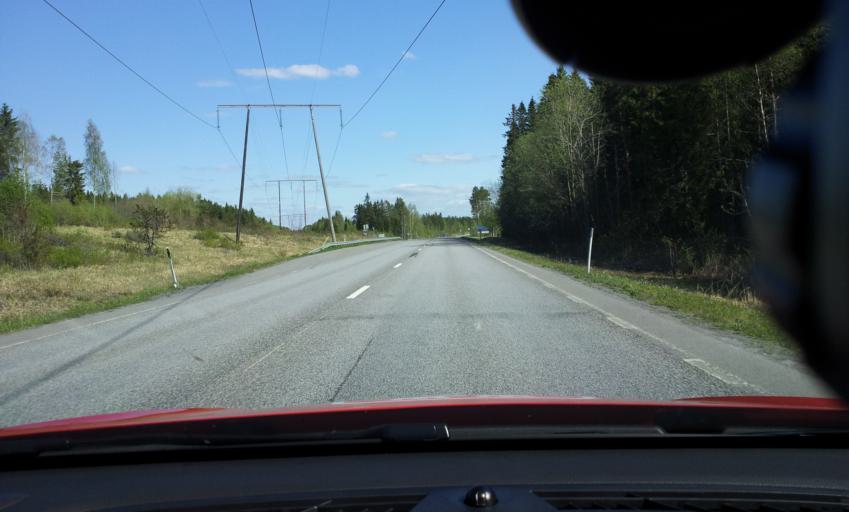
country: SE
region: Jaemtland
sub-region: Krokoms Kommun
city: Valla
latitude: 63.3356
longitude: 14.0135
